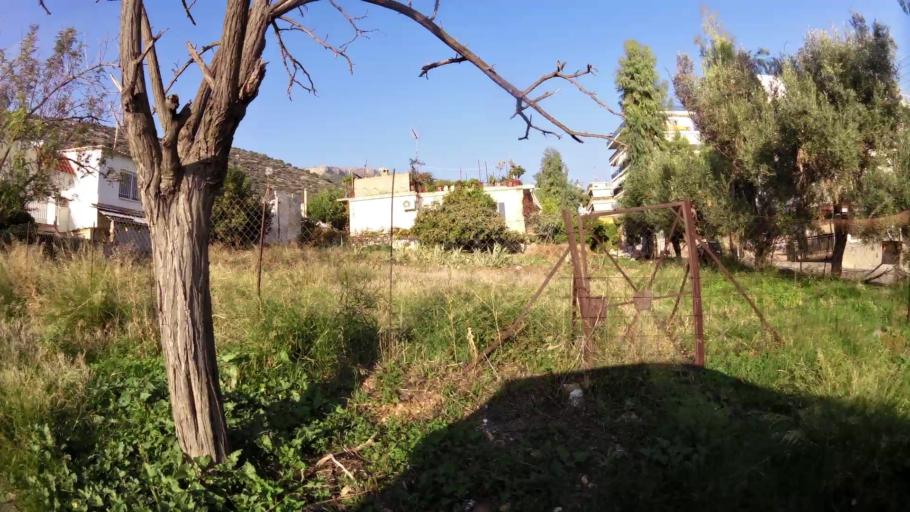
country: GR
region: Attica
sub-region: Nomarchia Athinas
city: Argyroupoli
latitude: 37.9023
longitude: 23.7681
